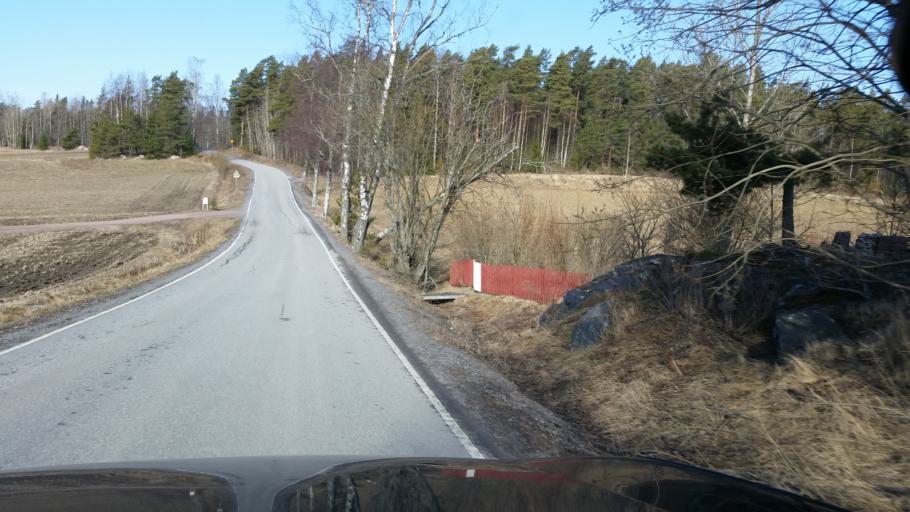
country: FI
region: Uusimaa
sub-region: Raaseporin
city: Inga
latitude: 60.0507
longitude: 24.0467
